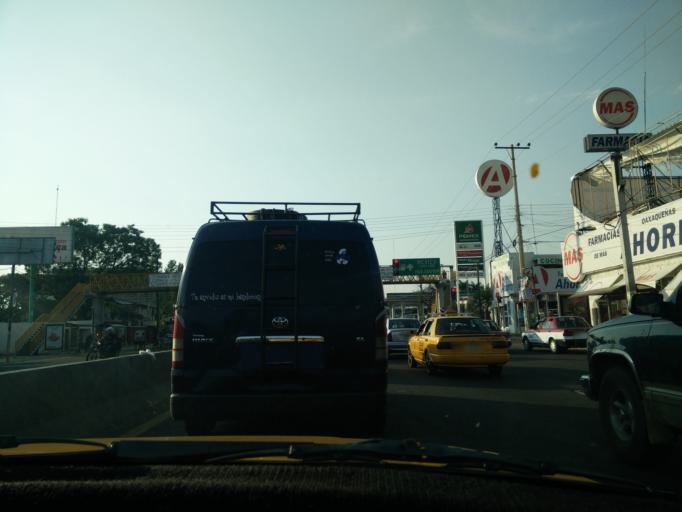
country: MX
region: Oaxaca
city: Oaxaca de Juarez
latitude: 17.0825
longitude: -96.7435
